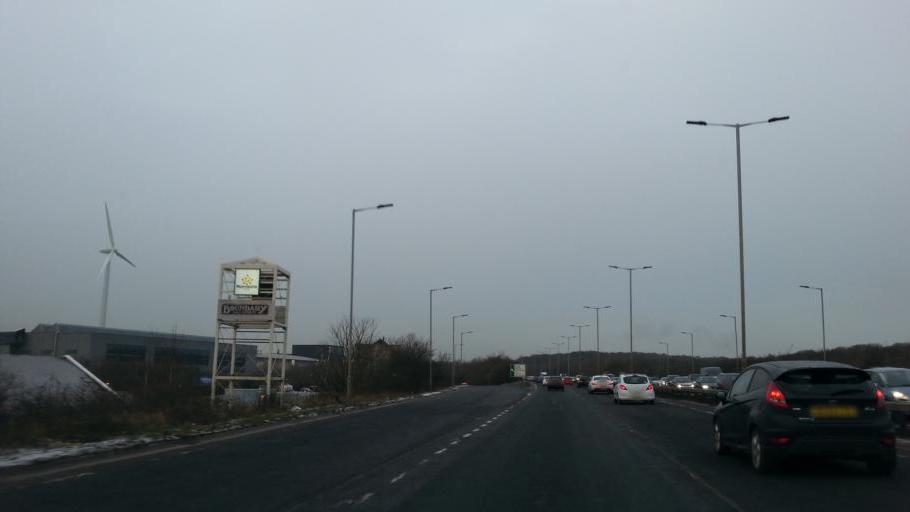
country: GB
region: England
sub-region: Rotherham
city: Orgreave
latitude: 53.3918
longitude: -1.3746
